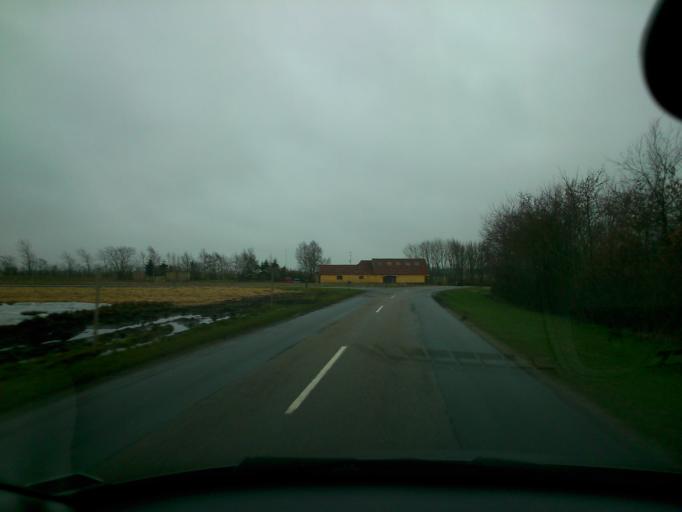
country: DK
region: Central Jutland
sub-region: Ringkobing-Skjern Kommune
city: Ringkobing
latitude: 56.1005
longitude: 8.4129
